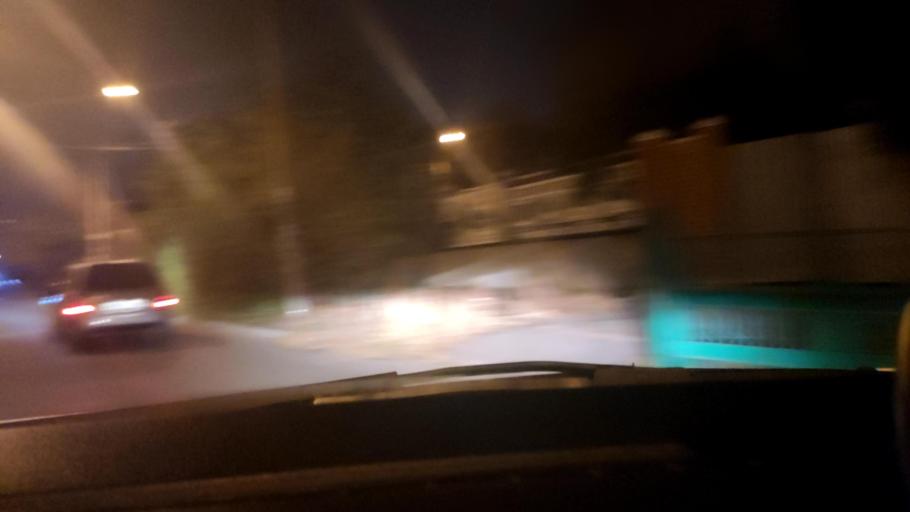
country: RU
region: Voronezj
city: Voronezh
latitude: 51.7078
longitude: 39.1987
